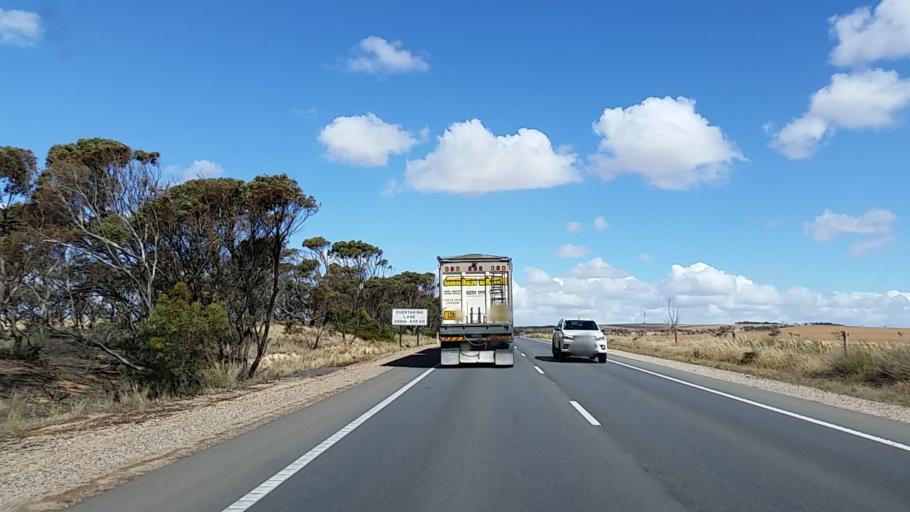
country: AU
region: South Australia
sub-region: Wakefield
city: Balaklava
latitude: -33.9610
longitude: 138.1789
